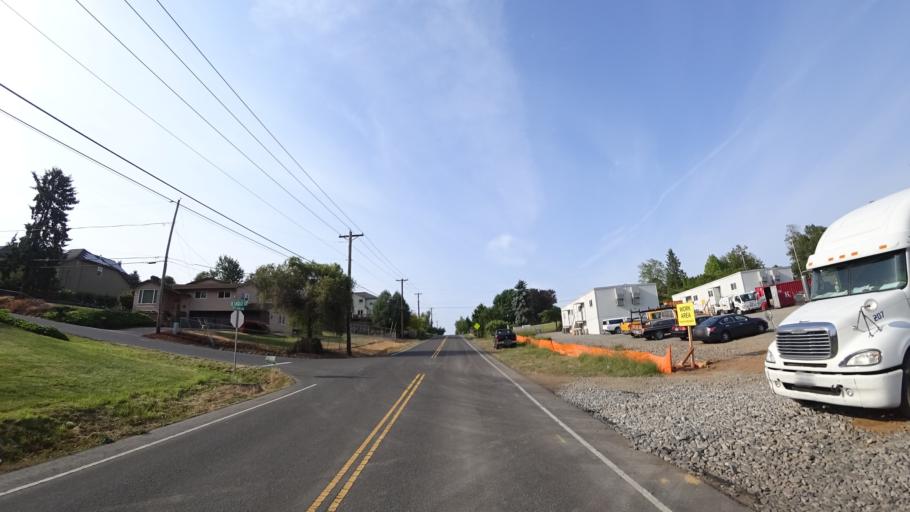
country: US
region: Oregon
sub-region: Clackamas County
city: Happy Valley
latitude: 45.4584
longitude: -122.5276
